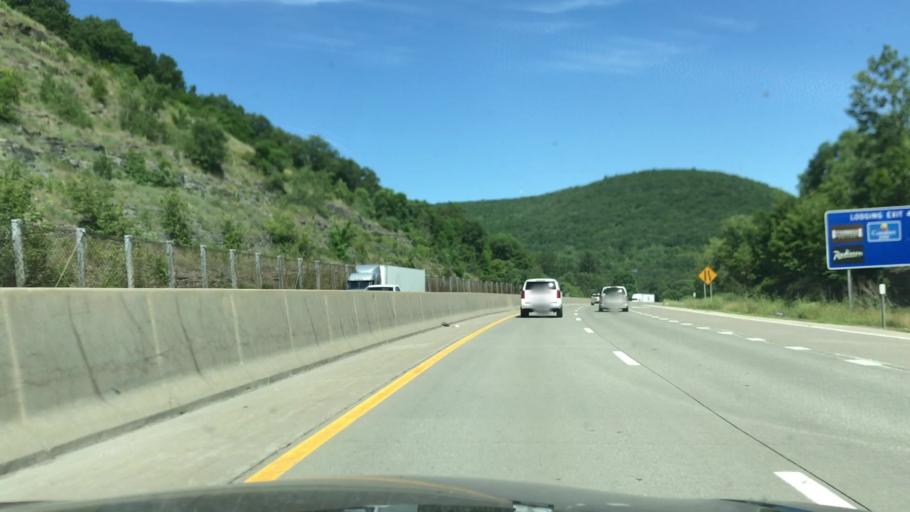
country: US
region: New York
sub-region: Steuben County
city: Corning
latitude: 42.1635
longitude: -77.0636
